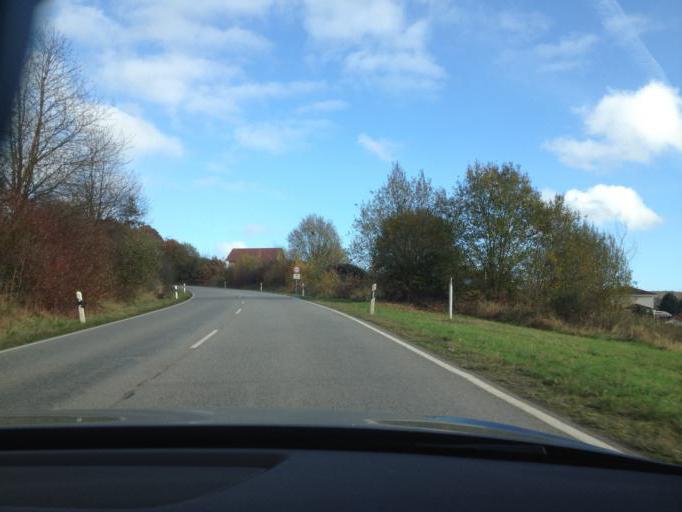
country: DE
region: Saarland
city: Sankt Wendel
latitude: 49.4526
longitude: 7.1711
